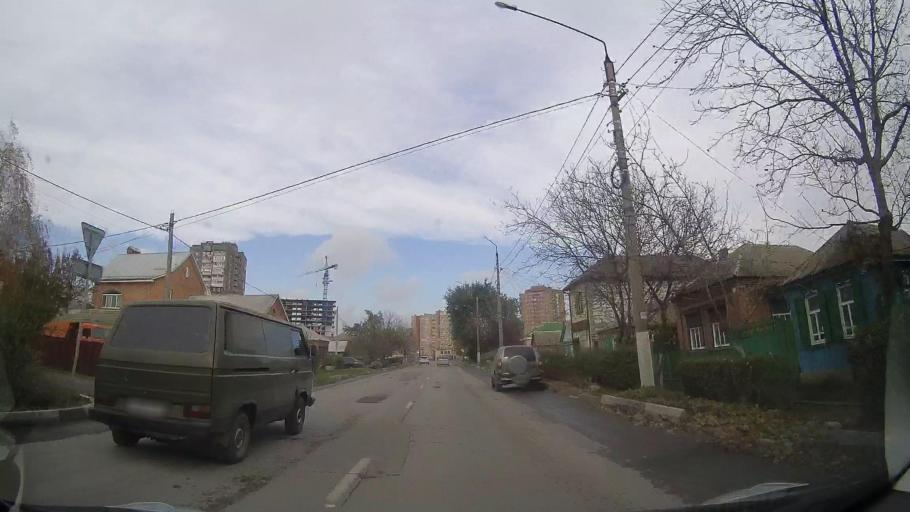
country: RU
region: Rostov
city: Bataysk
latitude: 47.1539
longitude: 39.7468
